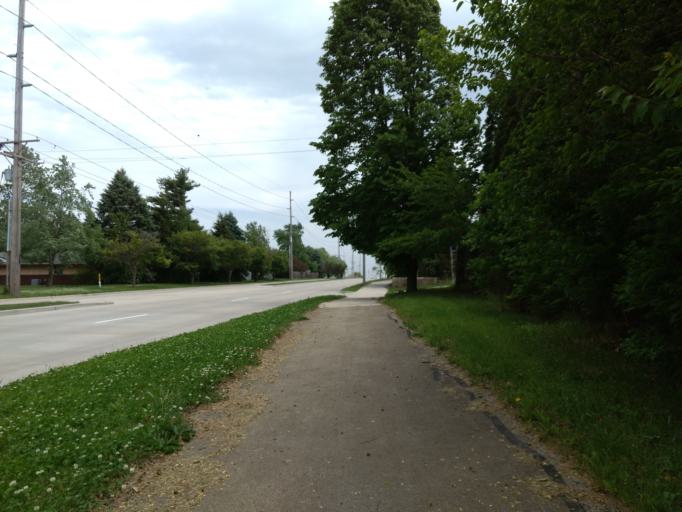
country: US
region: Illinois
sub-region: Champaign County
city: Urbana
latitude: 40.0837
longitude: -88.1956
